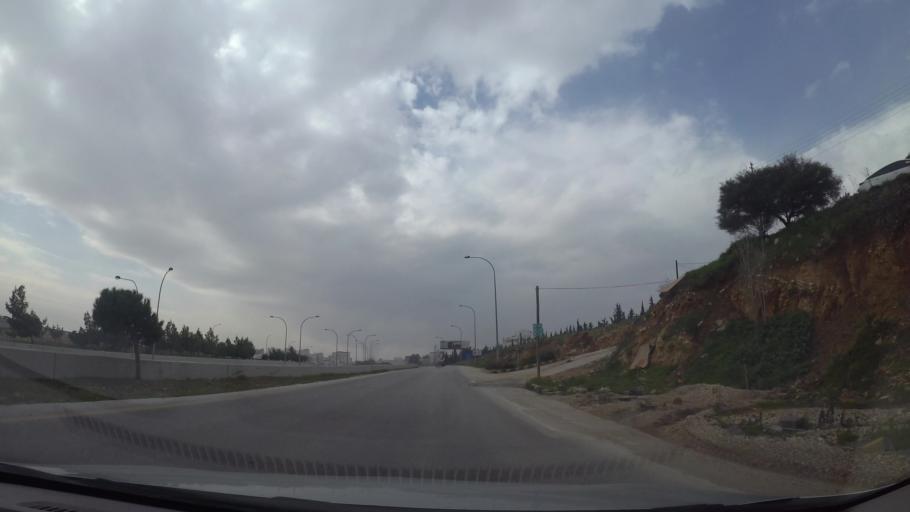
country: JO
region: Amman
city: Umm as Summaq
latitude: 31.9131
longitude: 35.8575
